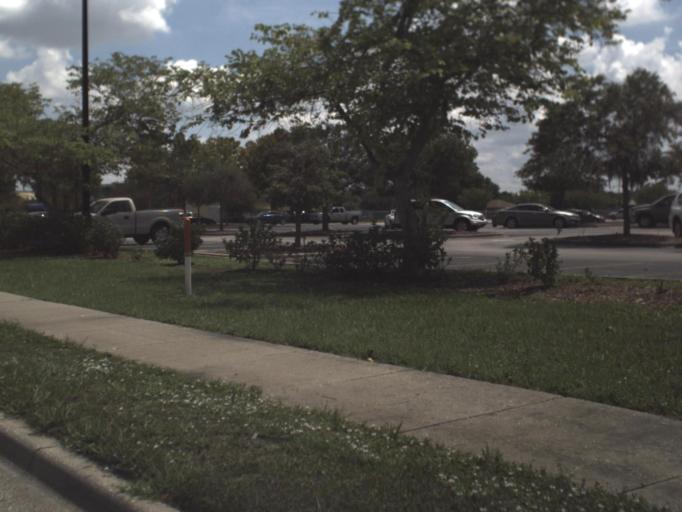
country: US
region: Florida
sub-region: Manatee County
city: South Bradenton
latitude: 27.4625
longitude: -82.6152
